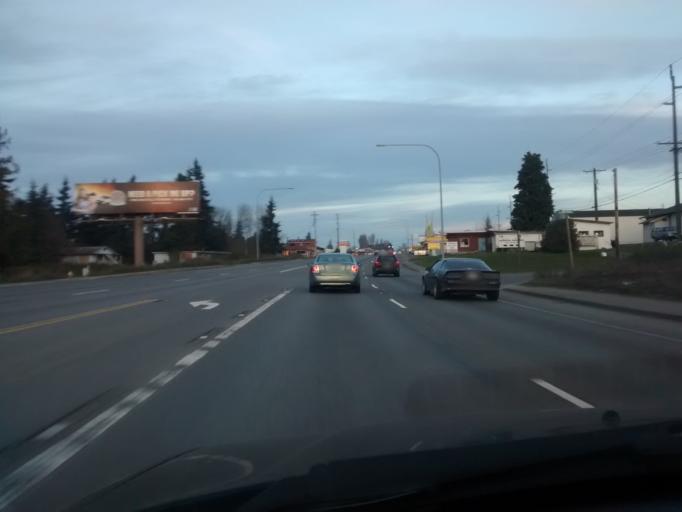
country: US
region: Washington
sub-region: Clallam County
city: Port Angeles East
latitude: 48.1047
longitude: -123.3791
